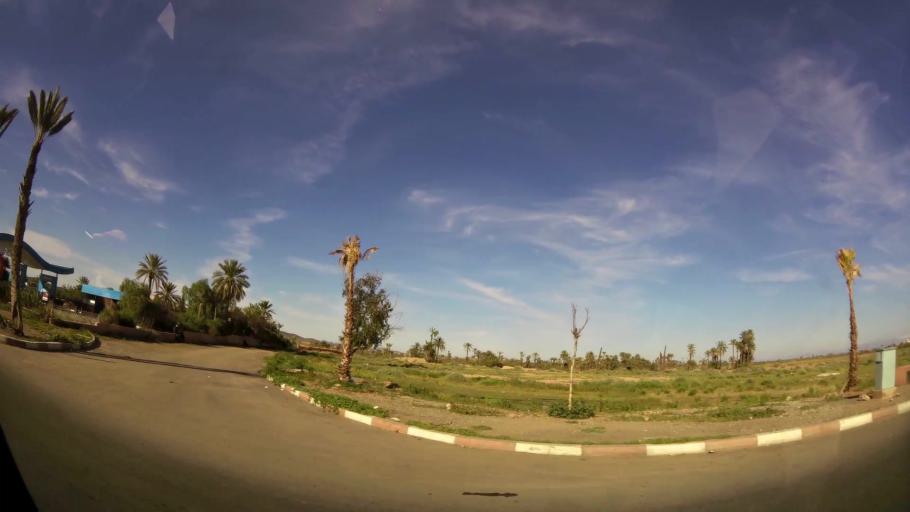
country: MA
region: Marrakech-Tensift-Al Haouz
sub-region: Marrakech
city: Marrakesh
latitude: 31.6924
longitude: -8.0561
